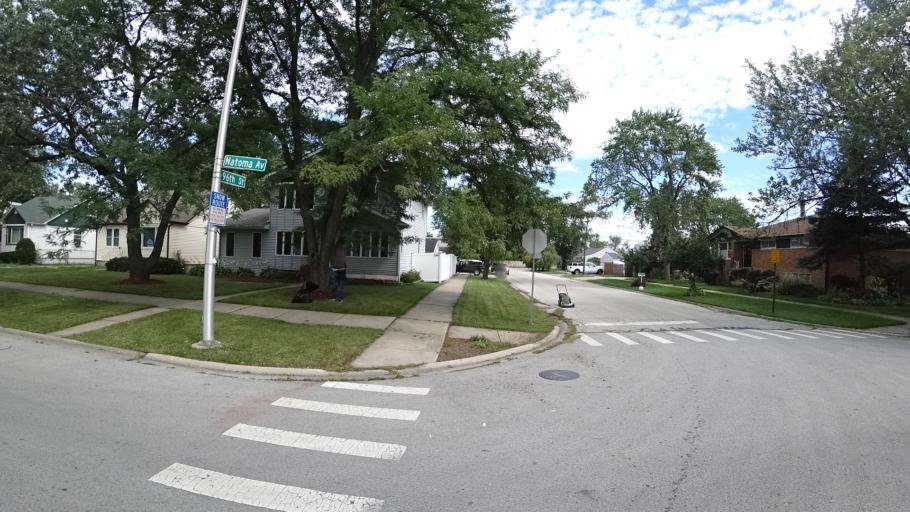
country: US
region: Illinois
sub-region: Cook County
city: Burbank
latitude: 41.7177
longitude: -87.7859
